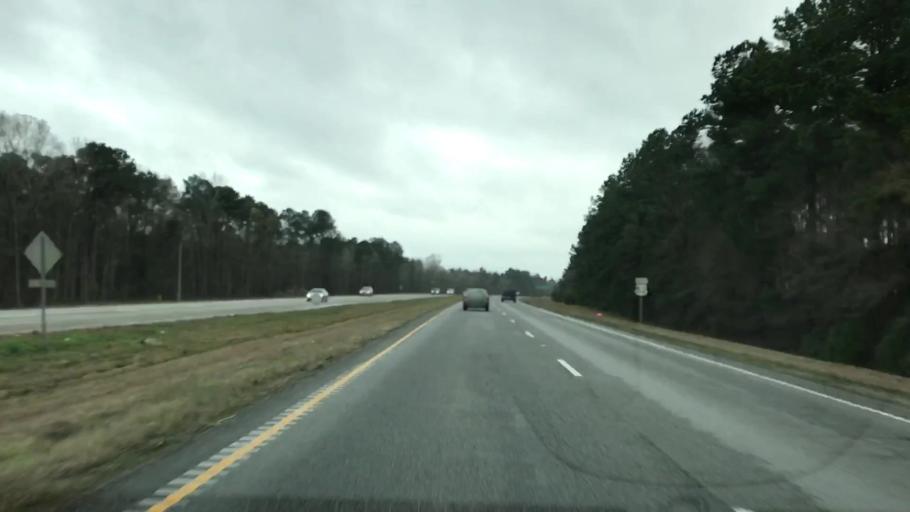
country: US
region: South Carolina
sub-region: Berkeley County
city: Moncks Corner
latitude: 33.1230
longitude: -80.0289
